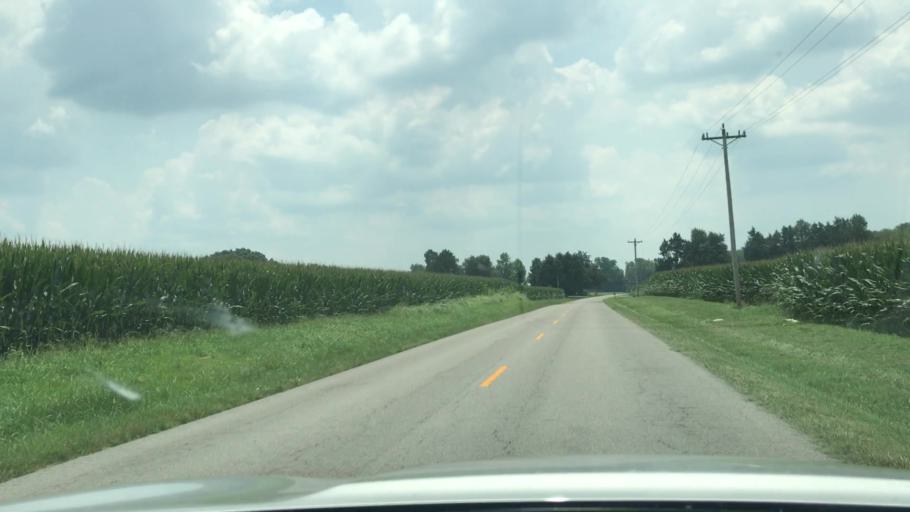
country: US
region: Kentucky
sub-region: Todd County
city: Elkton
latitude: 36.7460
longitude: -87.0952
